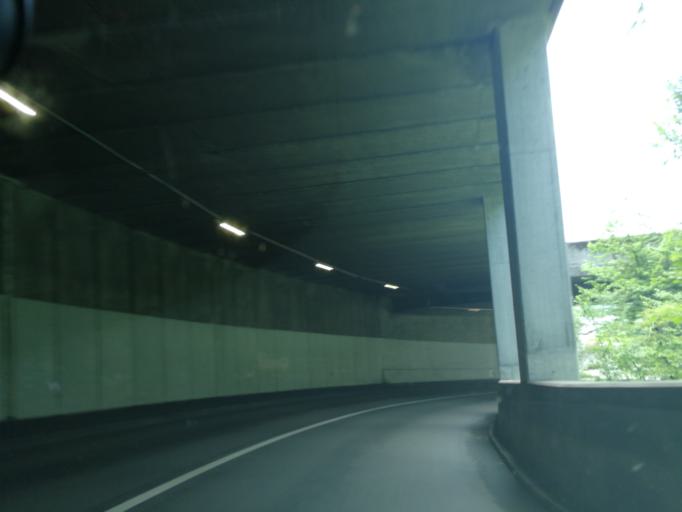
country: CH
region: Zurich
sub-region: Bezirk Meilen
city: Herrliberg
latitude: 47.2835
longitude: 8.6118
